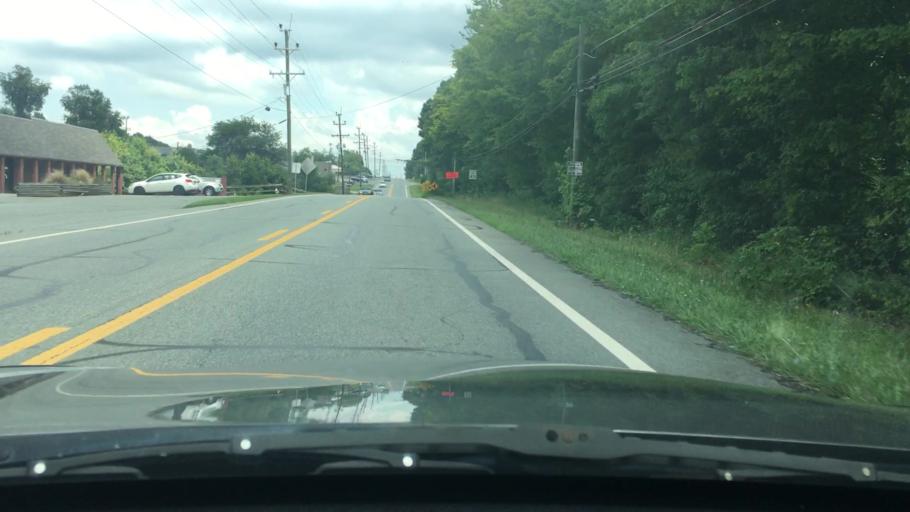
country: US
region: North Carolina
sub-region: Alamance County
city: Mebane
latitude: 36.0985
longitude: -79.2862
